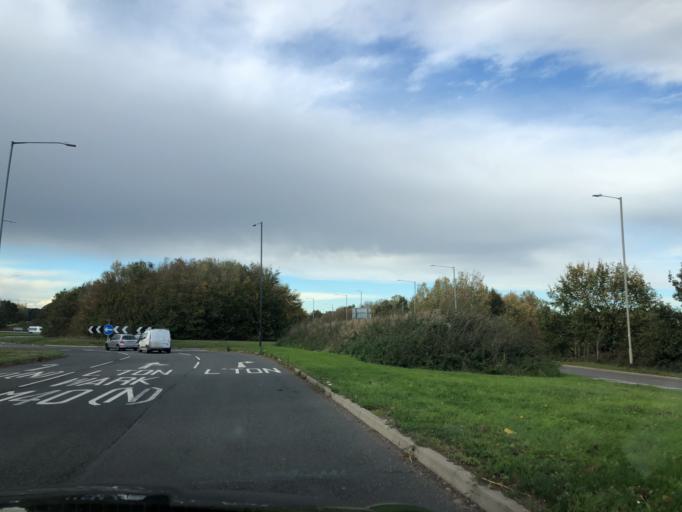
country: GB
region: England
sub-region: Warwickshire
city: Warwick
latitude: 52.2549
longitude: -1.5632
